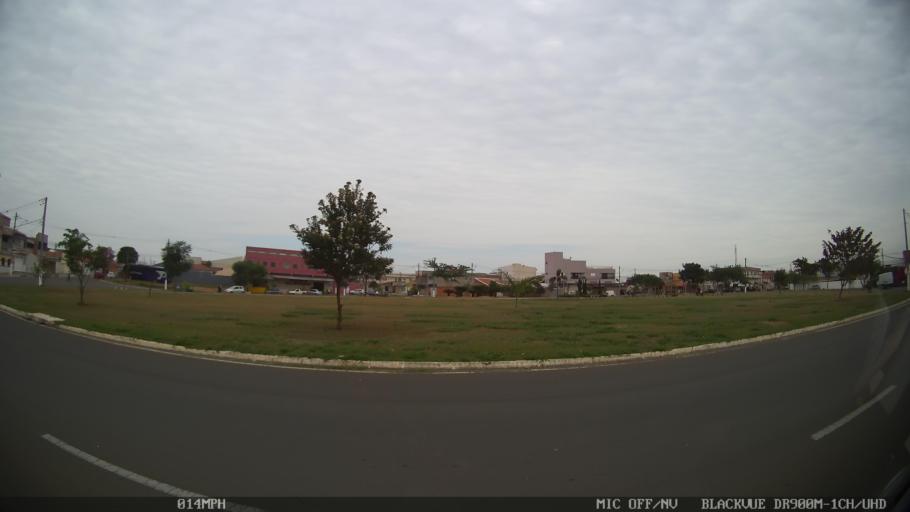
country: BR
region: Sao Paulo
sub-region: Paulinia
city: Paulinia
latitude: -22.7153
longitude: -47.1685
